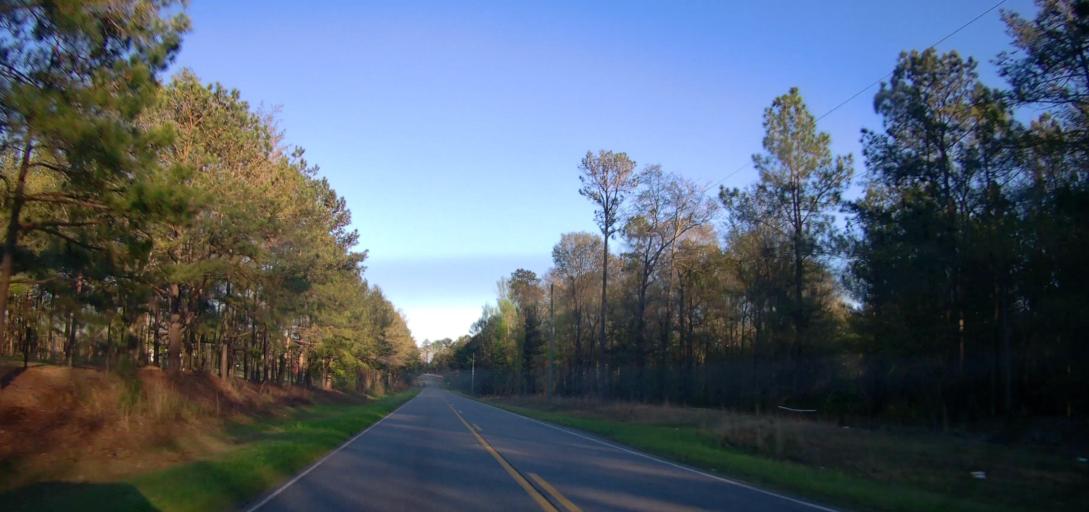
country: US
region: Georgia
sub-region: Wilkinson County
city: Gordon
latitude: 32.8798
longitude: -83.2754
